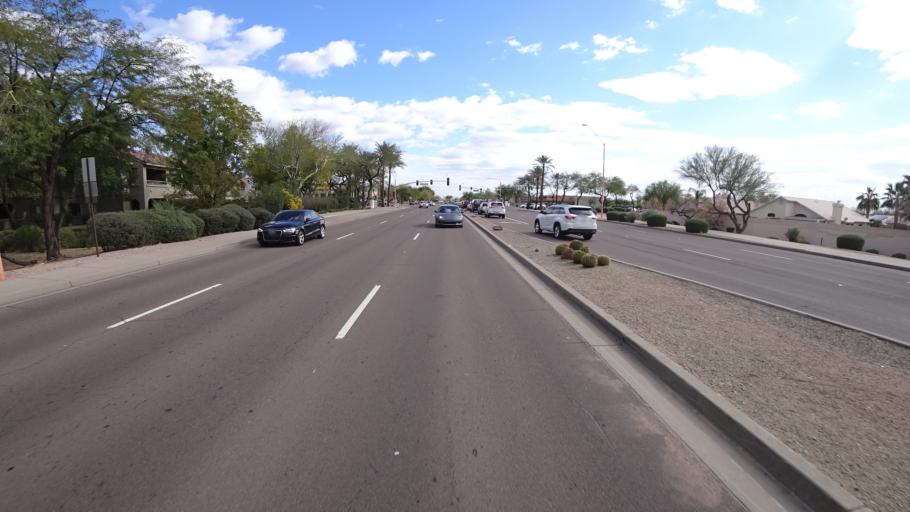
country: US
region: Arizona
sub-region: Maricopa County
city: Paradise Valley
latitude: 33.6226
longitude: -111.8760
